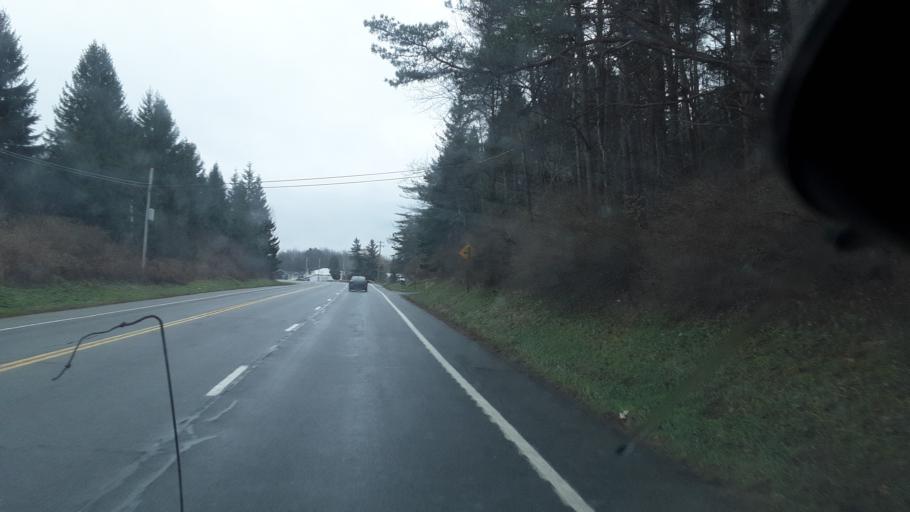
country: US
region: New York
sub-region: Erie County
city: Holland
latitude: 42.5930
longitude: -78.4962
